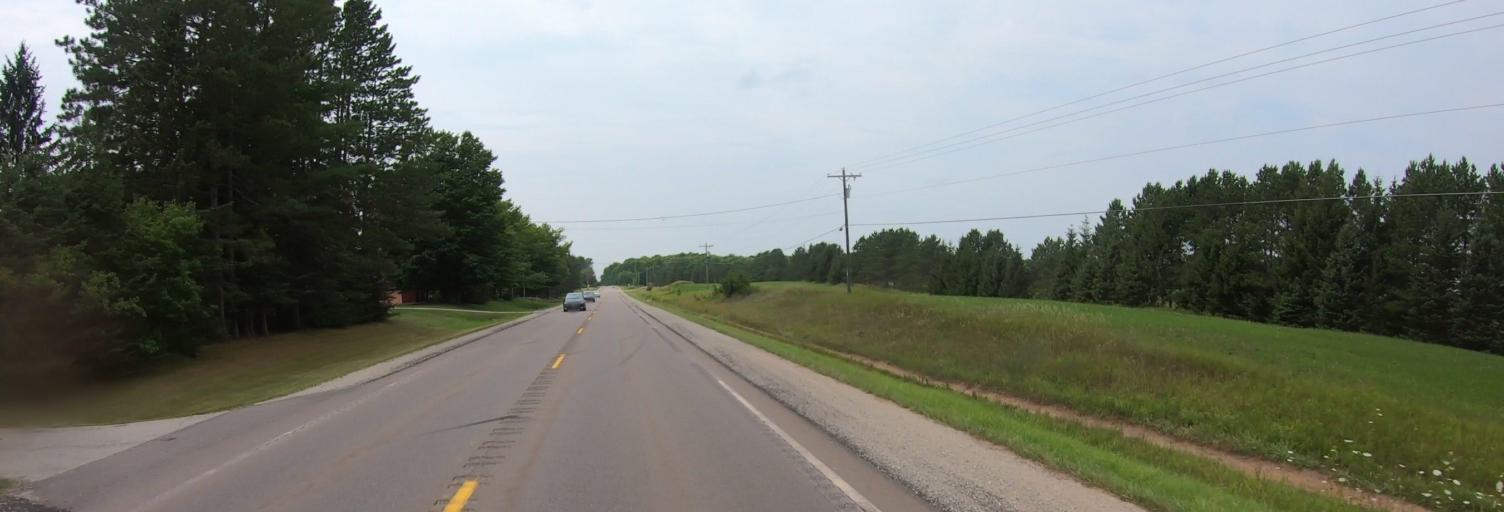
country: US
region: Michigan
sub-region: Alger County
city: Munising
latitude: 46.3549
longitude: -86.9867
